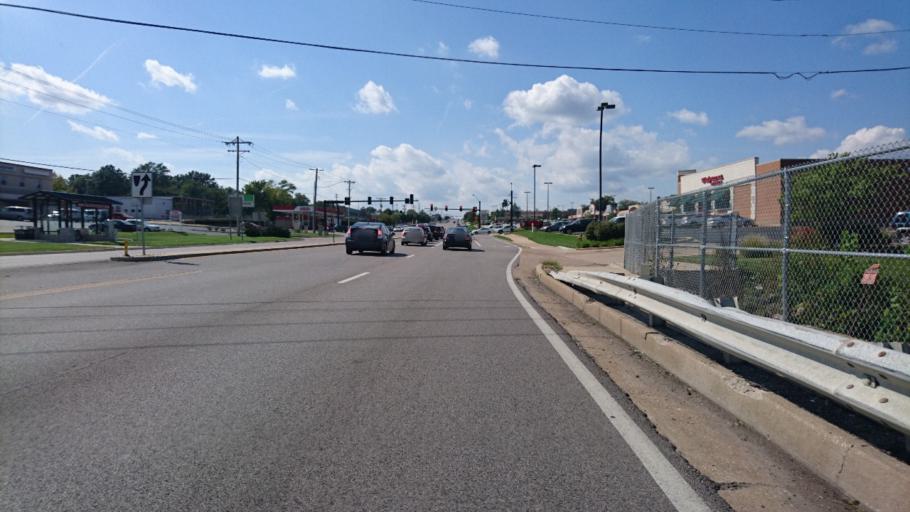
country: US
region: Missouri
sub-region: Saint Louis County
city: Ballwin
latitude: 38.5930
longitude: -90.5562
